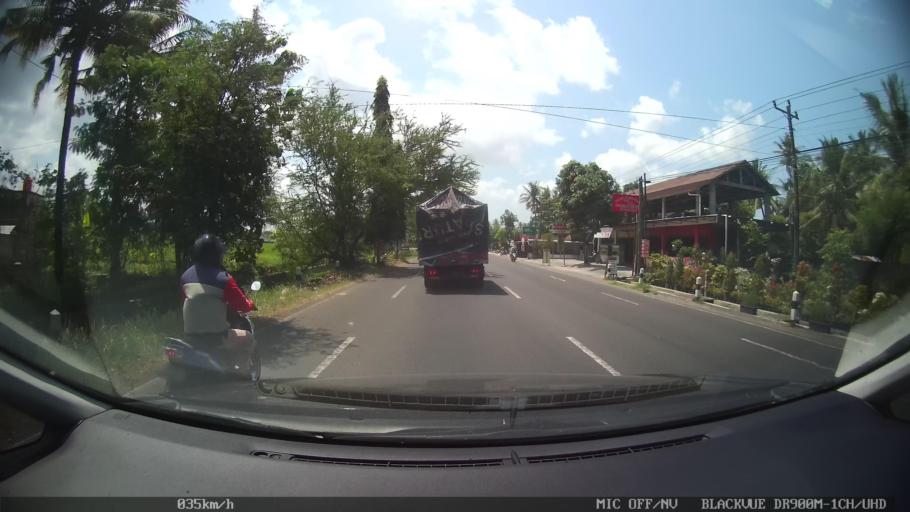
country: ID
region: Daerah Istimewa Yogyakarta
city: Pandak
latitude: -7.9121
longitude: 110.2896
